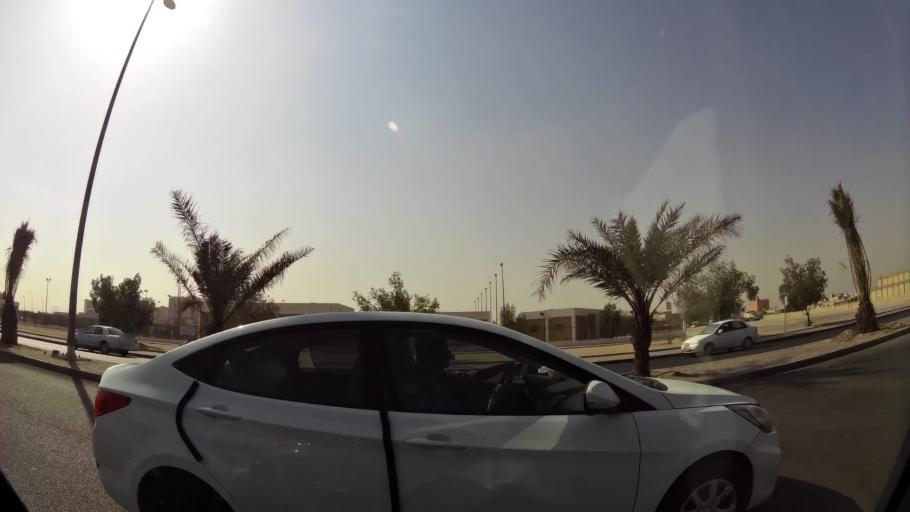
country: KW
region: Al Ahmadi
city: Al Manqaf
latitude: 29.1045
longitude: 48.1241
